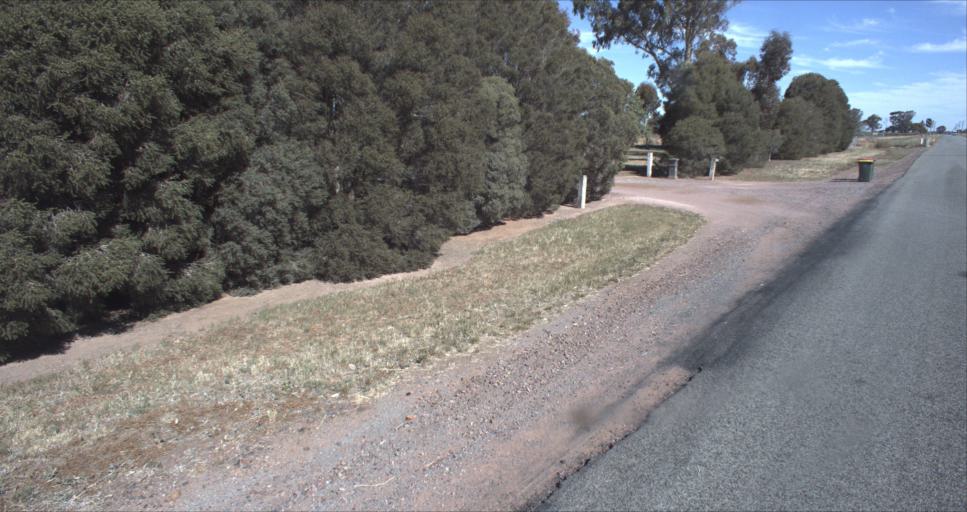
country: AU
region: New South Wales
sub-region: Leeton
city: Leeton
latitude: -34.5689
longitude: 146.3821
